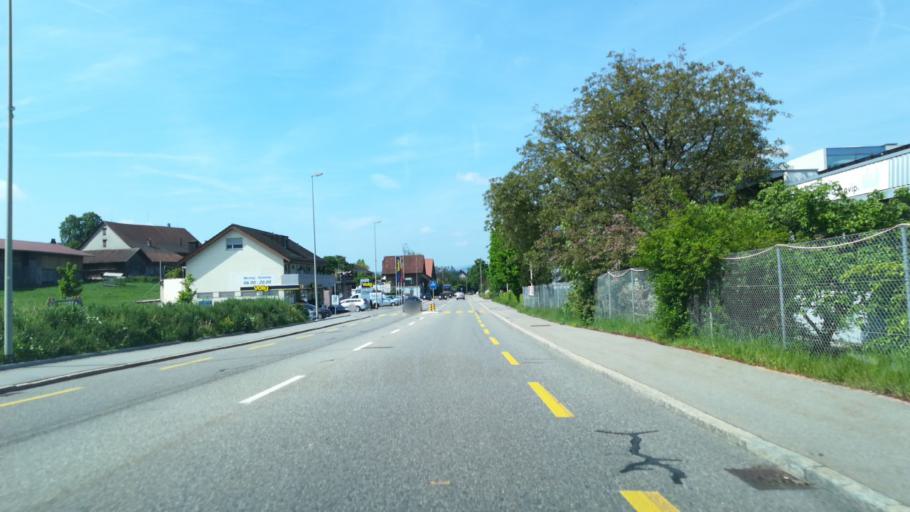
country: CH
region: Zurich
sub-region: Bezirk Pfaeffikon
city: Tagelswangen
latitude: 47.4318
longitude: 8.6749
